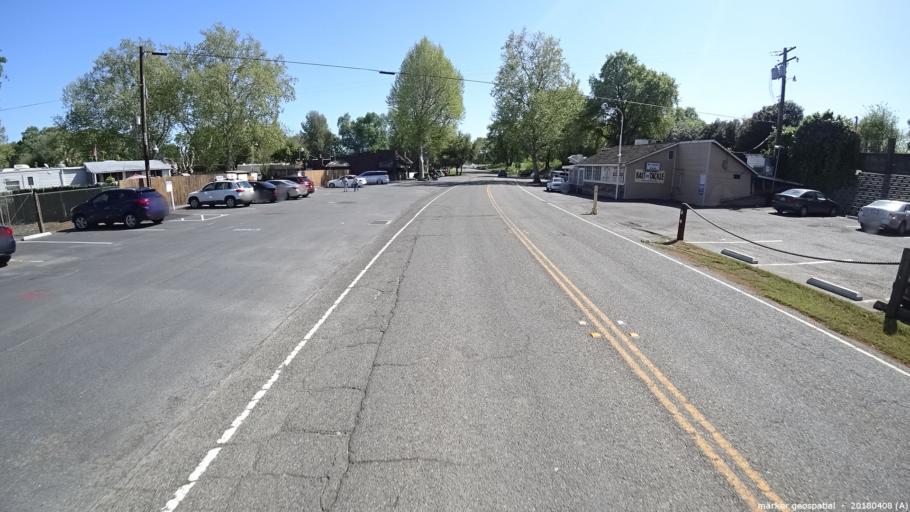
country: US
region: California
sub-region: Sacramento County
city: Parkway
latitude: 38.4585
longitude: -121.5010
